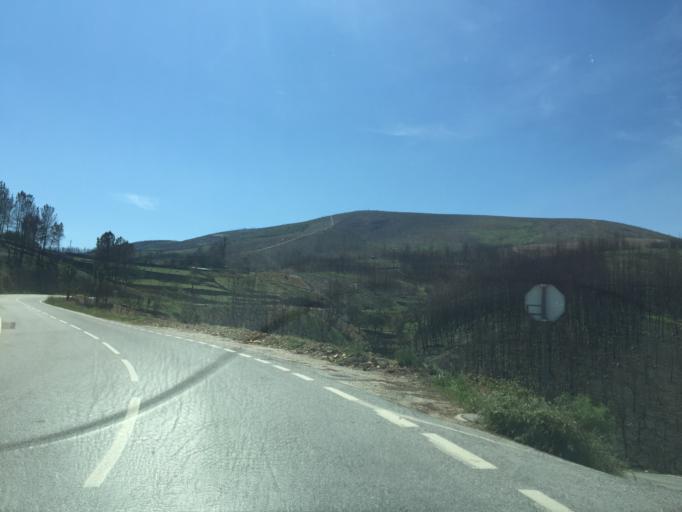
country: PT
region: Coimbra
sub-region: Pampilhosa da Serra
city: Pampilhosa da Serra
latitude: 40.0438
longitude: -7.9567
